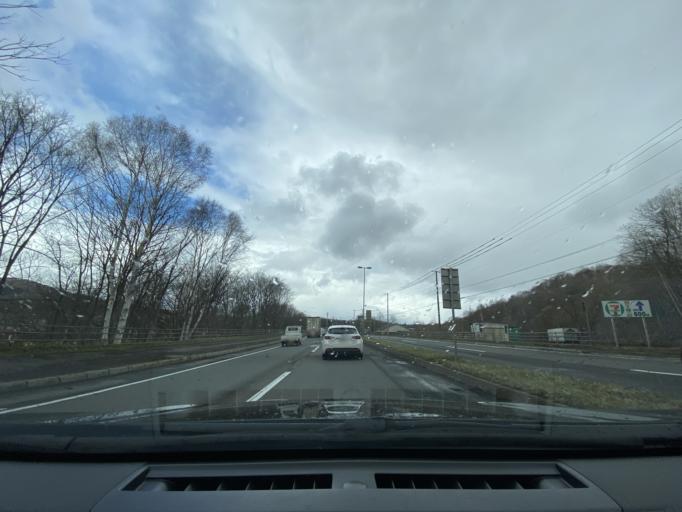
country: JP
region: Hokkaido
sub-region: Asahikawa-shi
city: Asahikawa
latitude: 43.7626
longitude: 142.2800
